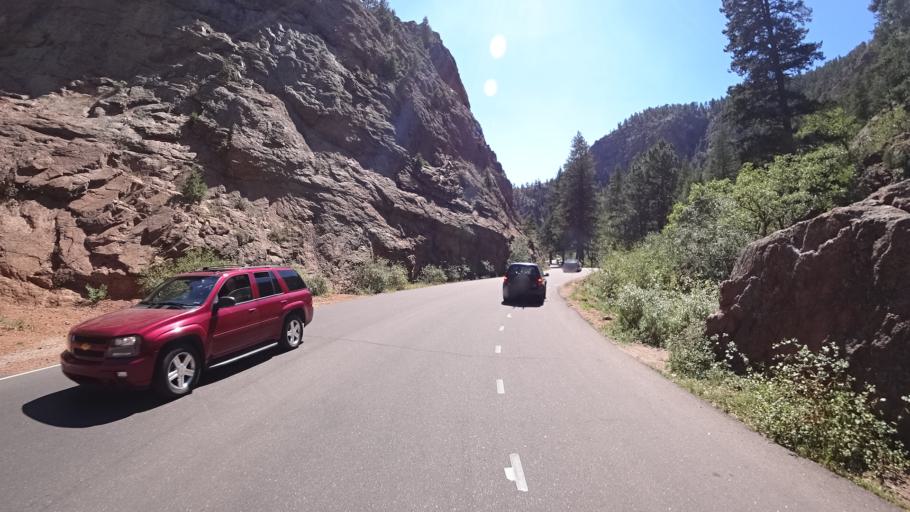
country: US
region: Colorado
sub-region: El Paso County
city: Colorado Springs
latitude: 38.7923
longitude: -104.8751
